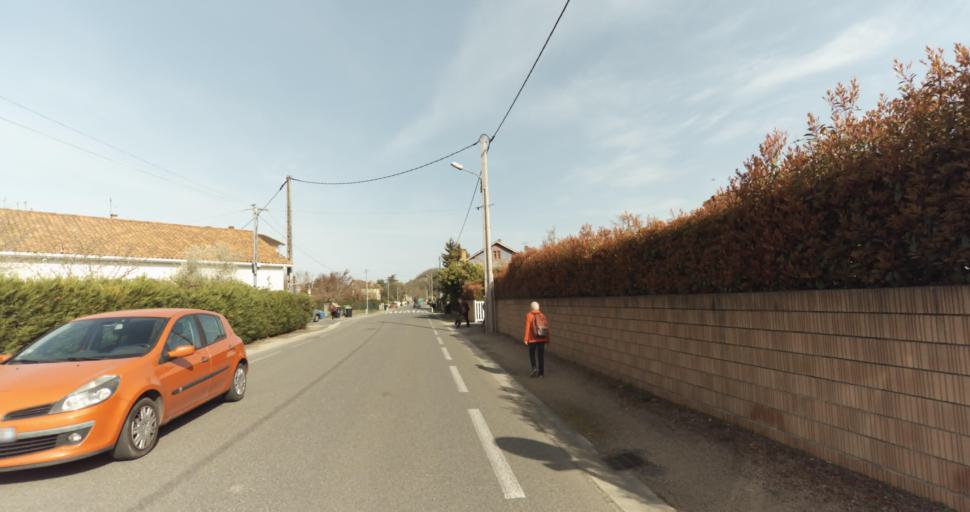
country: FR
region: Midi-Pyrenees
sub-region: Departement du Tarn
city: Saint-Sulpice-la-Pointe
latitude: 43.7804
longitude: 1.6811
